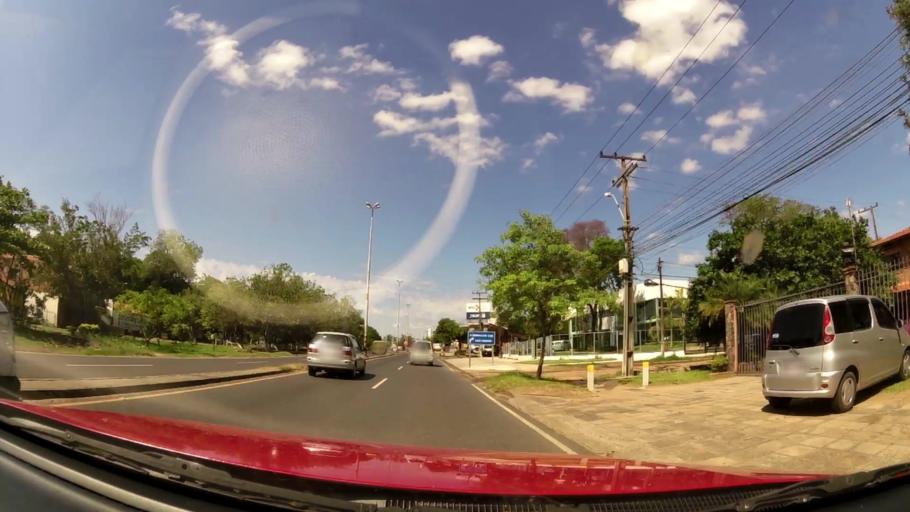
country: PY
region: Central
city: Colonia Mariano Roque Alonso
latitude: -25.2514
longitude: -57.5560
